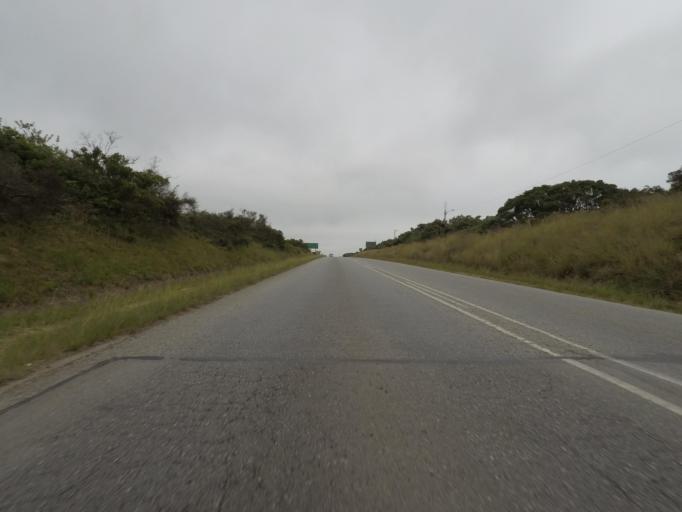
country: ZA
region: Eastern Cape
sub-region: Cacadu District Municipality
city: Port Alfred
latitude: -33.6801
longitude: 26.6632
